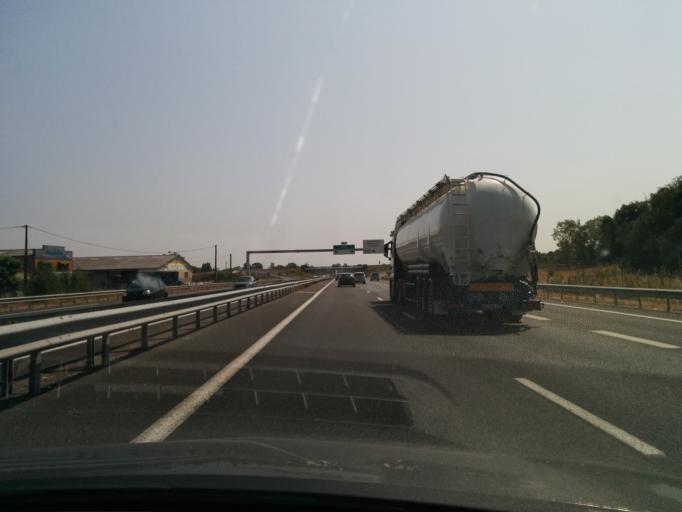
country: FR
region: Midi-Pyrenees
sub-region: Departement du Tarn
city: Castelnau-de-Levis
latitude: 43.9153
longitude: 2.0642
